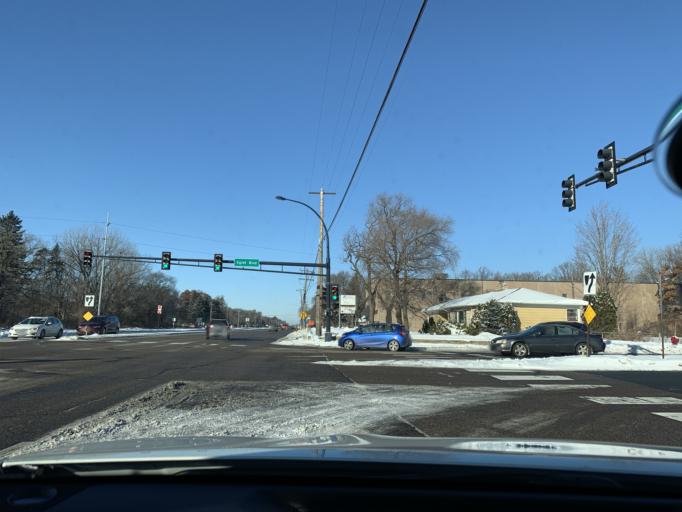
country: US
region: Minnesota
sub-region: Anoka County
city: Coon Rapids
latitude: 45.1548
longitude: -93.3060
